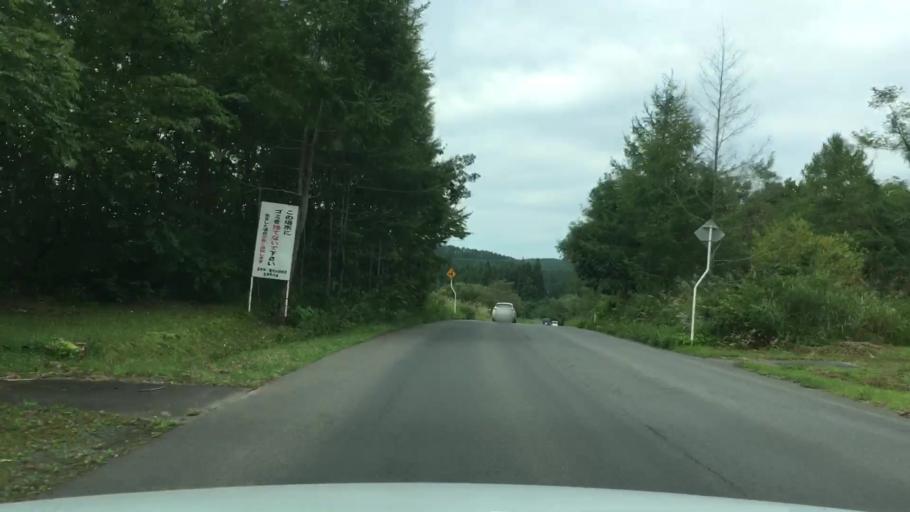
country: JP
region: Aomori
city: Shimokizukuri
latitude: 40.7129
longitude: 140.2656
